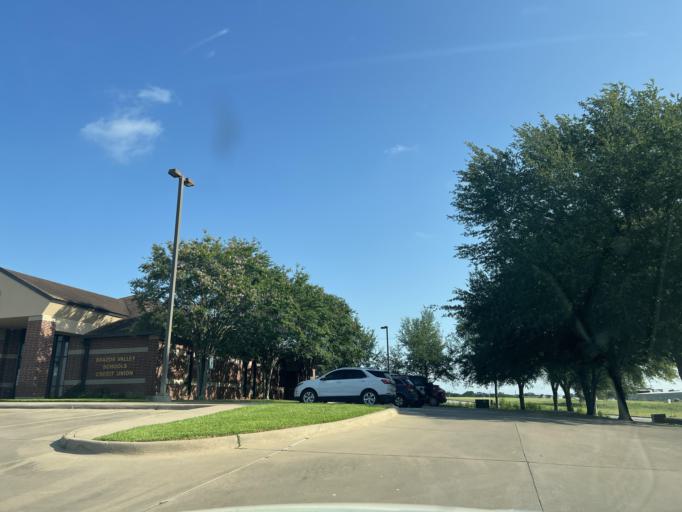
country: US
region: Texas
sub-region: Washington County
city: Brenham
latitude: 30.1460
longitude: -96.3849
